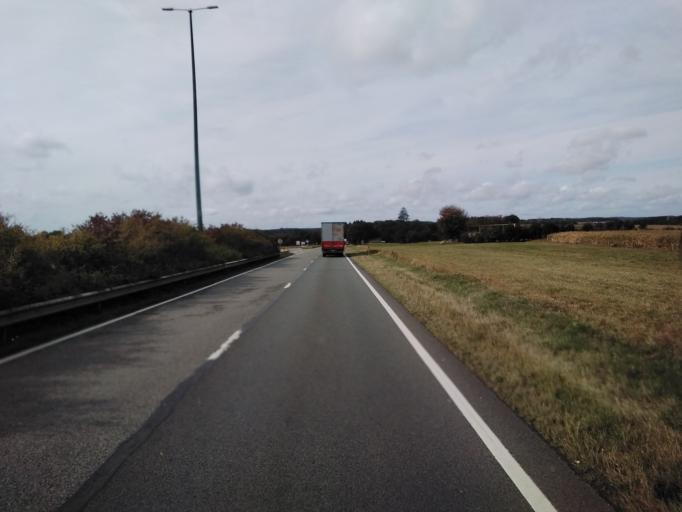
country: BE
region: Wallonia
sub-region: Province du Luxembourg
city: Bertrix
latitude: 49.8735
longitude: 5.2472
